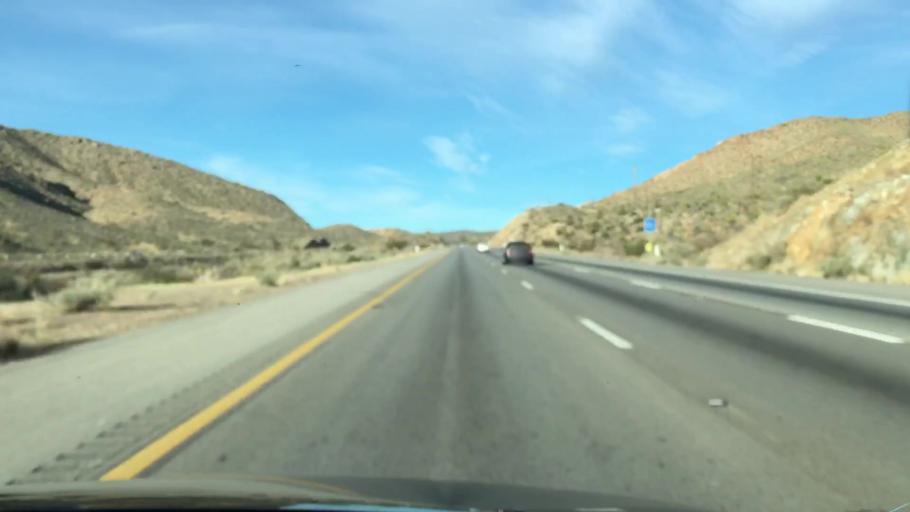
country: US
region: Nevada
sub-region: Clark County
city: Sandy Valley
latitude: 35.4699
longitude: -115.4950
